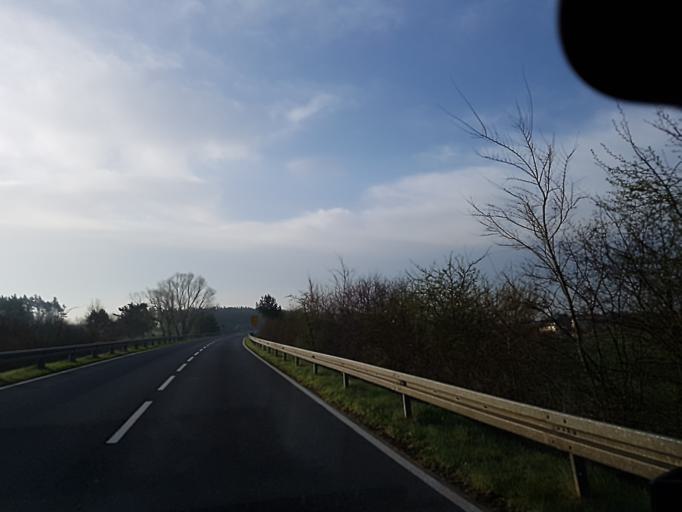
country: DE
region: Saxony
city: Riesa
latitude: 51.3474
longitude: 13.2941
